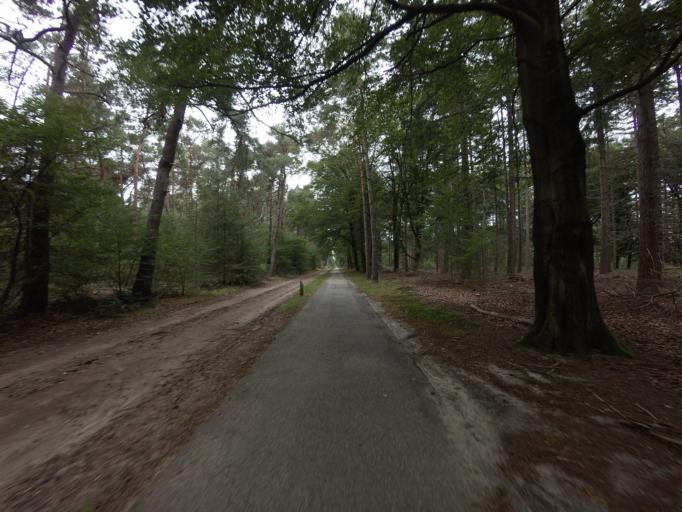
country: NL
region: Overijssel
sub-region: Gemeente Hof van Twente
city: Markelo
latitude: 52.3034
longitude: 6.4543
